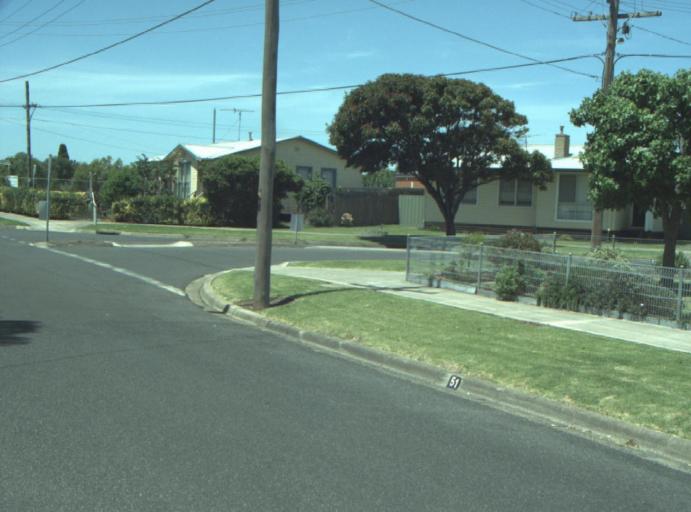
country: AU
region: Victoria
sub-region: Greater Geelong
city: Bell Park
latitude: -38.0854
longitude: 144.3509
